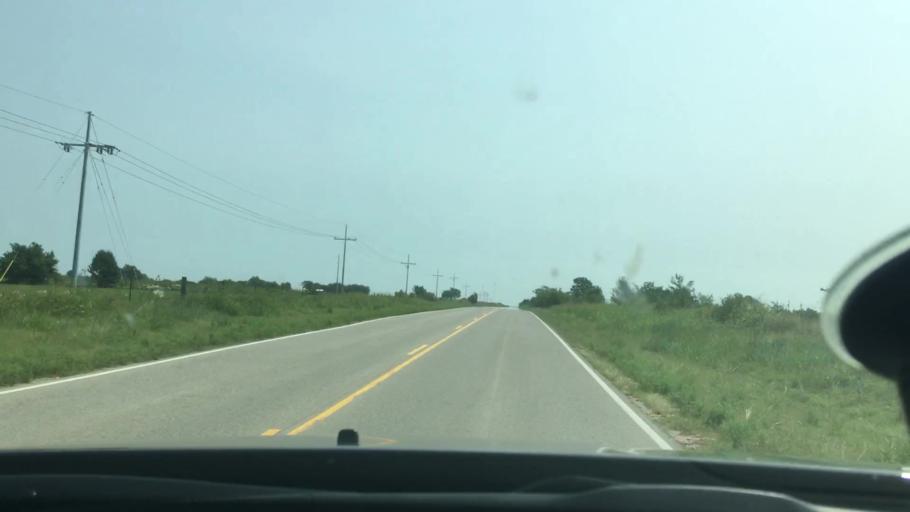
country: US
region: Oklahoma
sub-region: Garvin County
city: Stratford
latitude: 34.7967
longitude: -96.9170
